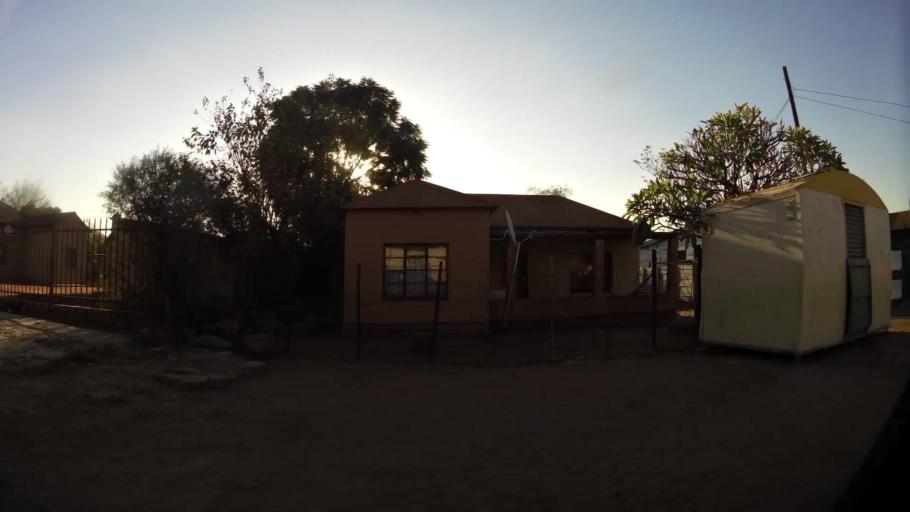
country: ZA
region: North-West
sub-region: Bojanala Platinum District Municipality
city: Rustenburg
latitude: -25.6455
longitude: 27.2181
